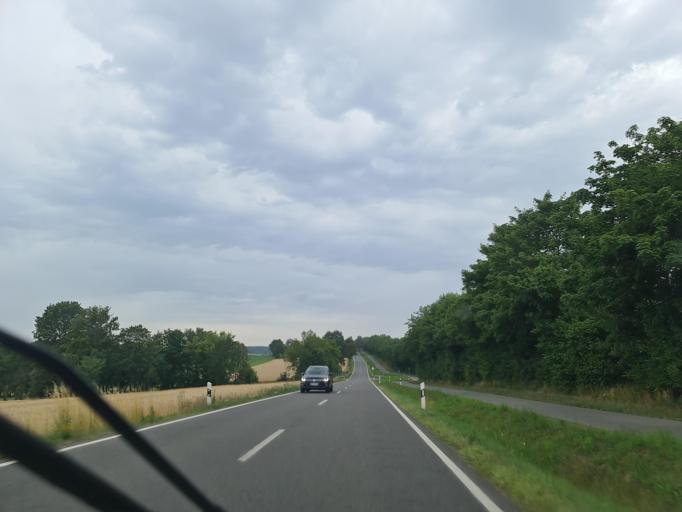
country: DE
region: Saxony
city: Eppendorf
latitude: 50.7926
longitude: 13.2540
